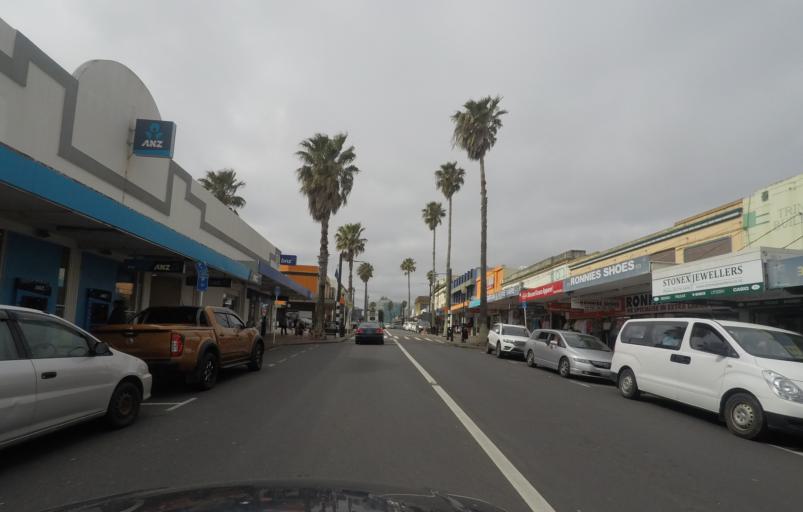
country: NZ
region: Auckland
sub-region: Auckland
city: Mangere
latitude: -36.9437
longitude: 174.8432
